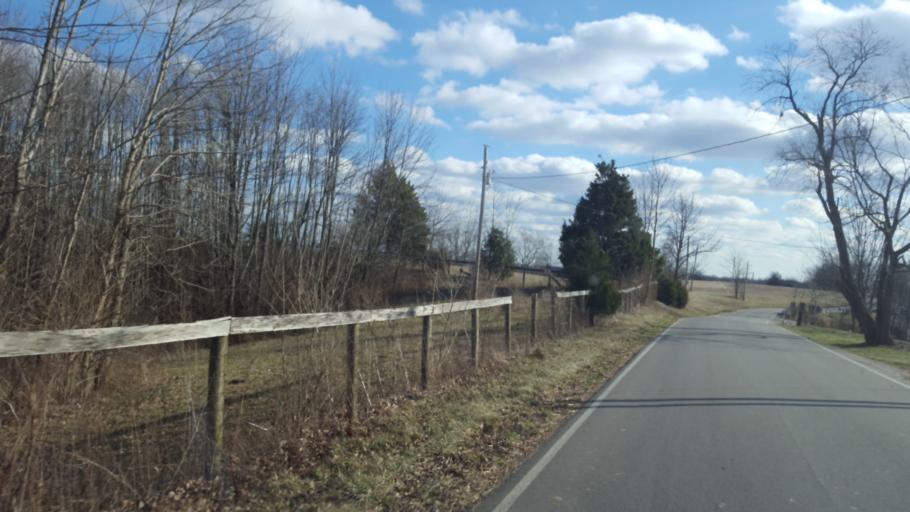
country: US
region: Kentucky
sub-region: Scott County
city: Georgetown
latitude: 38.2844
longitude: -84.5028
